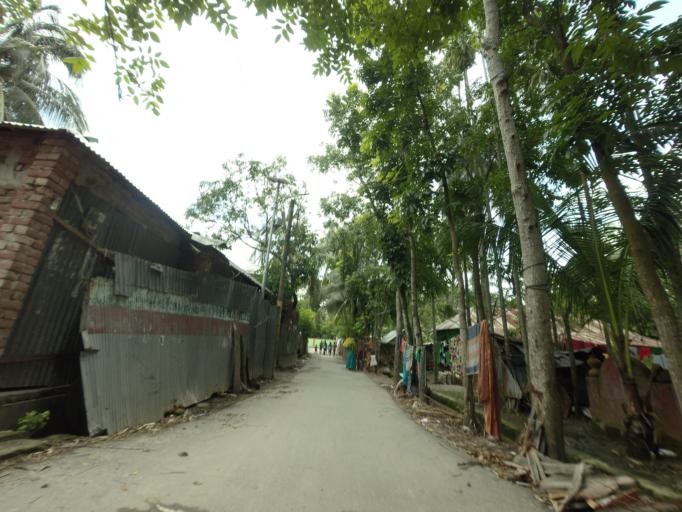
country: BD
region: Khulna
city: Kalia
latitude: 23.0408
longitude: 89.6330
